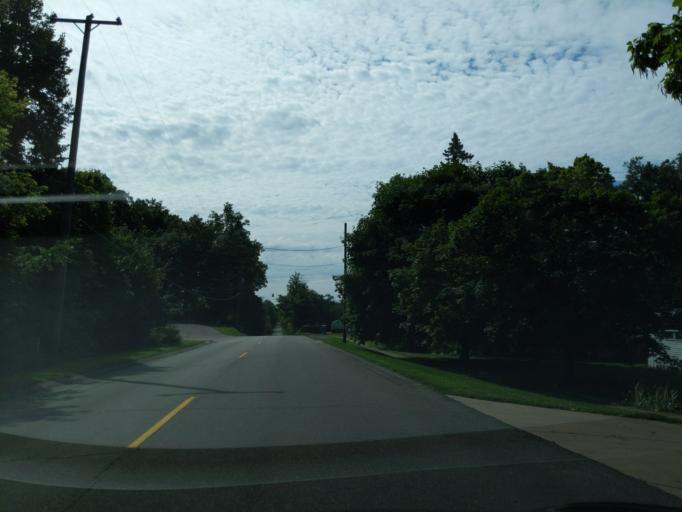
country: US
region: Michigan
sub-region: Barry County
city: Nashville
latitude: 42.6192
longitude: -85.0249
